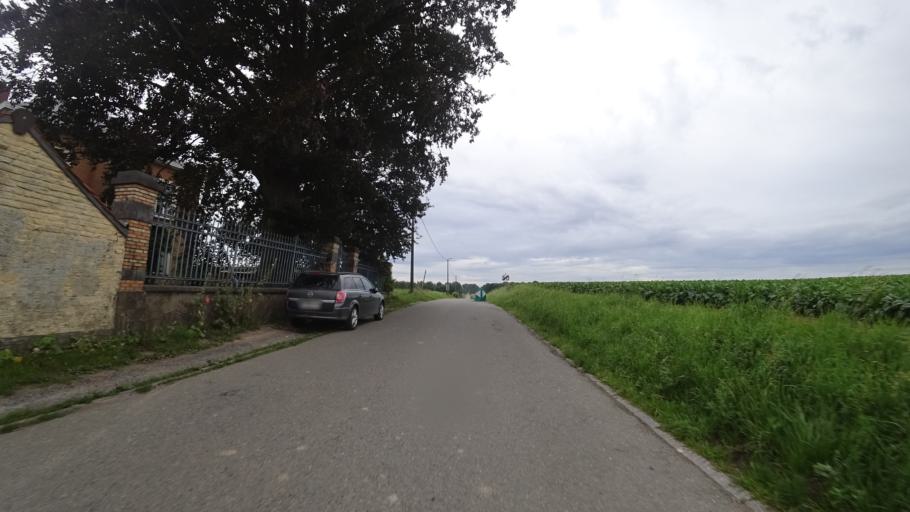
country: BE
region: Wallonia
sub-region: Province du Brabant Wallon
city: Walhain-Saint-Paul
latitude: 50.6012
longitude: 4.7484
